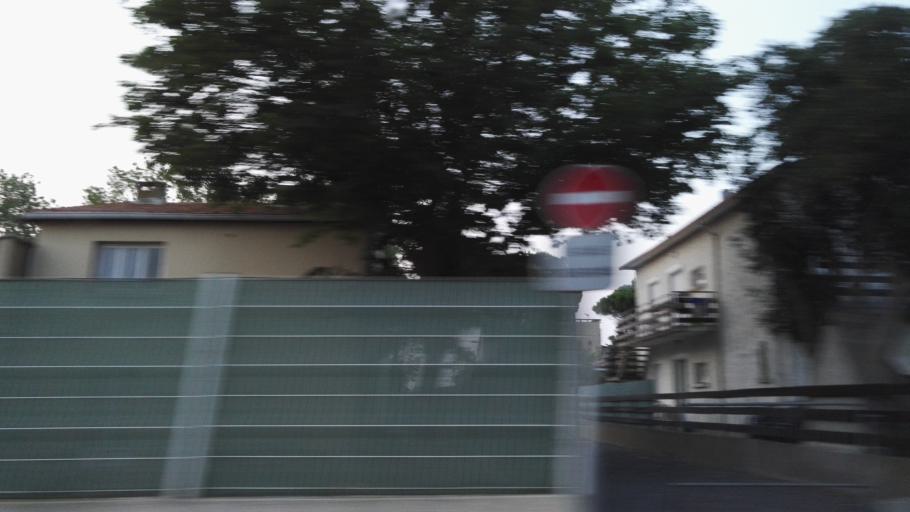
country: FR
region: Languedoc-Roussillon
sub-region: Departement de l'Herault
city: Marseillan
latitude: 43.3190
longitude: 3.5488
